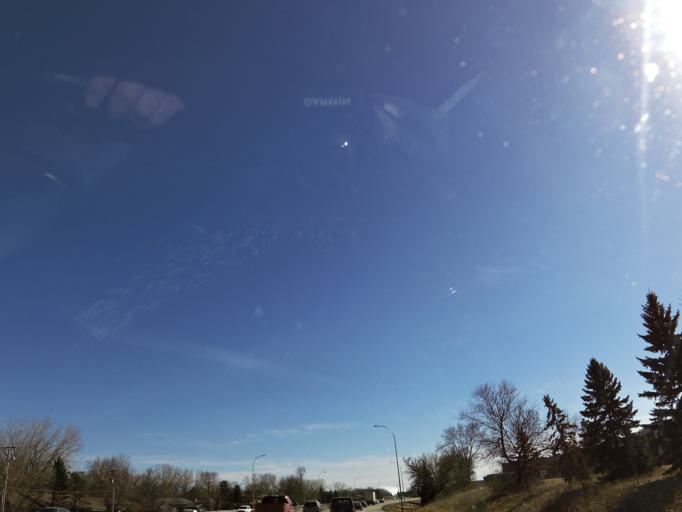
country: US
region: Minnesota
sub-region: Hennepin County
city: Edina
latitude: 44.8789
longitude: -93.3979
